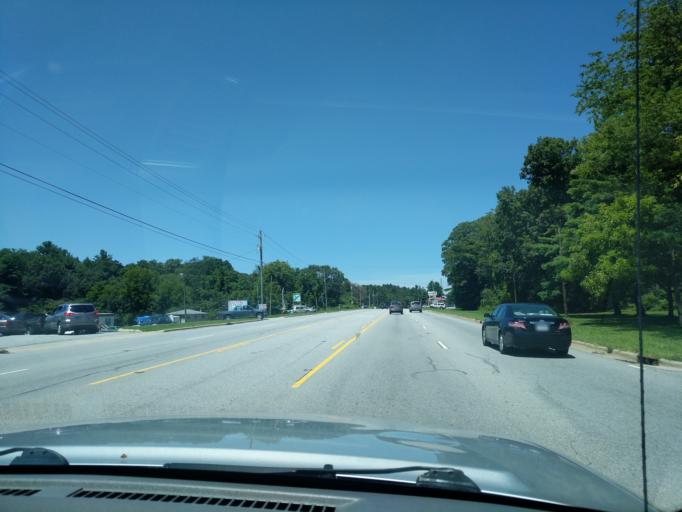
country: US
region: North Carolina
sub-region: Henderson County
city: Fletcher
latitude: 35.4490
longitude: -82.5086
